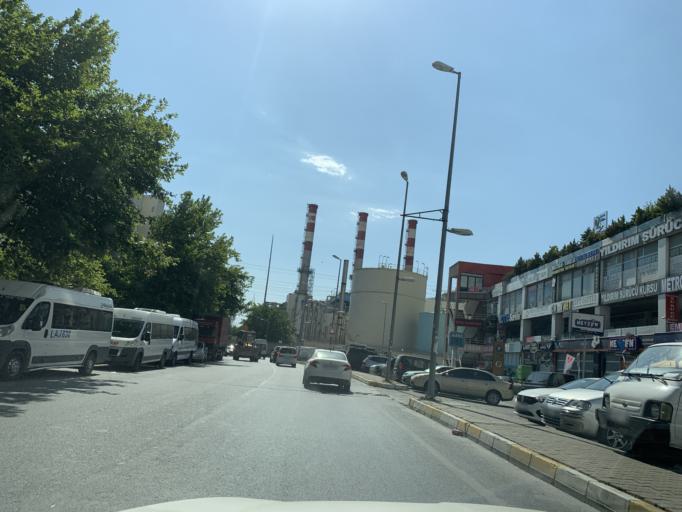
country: TR
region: Istanbul
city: Esenyurt
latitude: 41.0650
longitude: 28.6704
